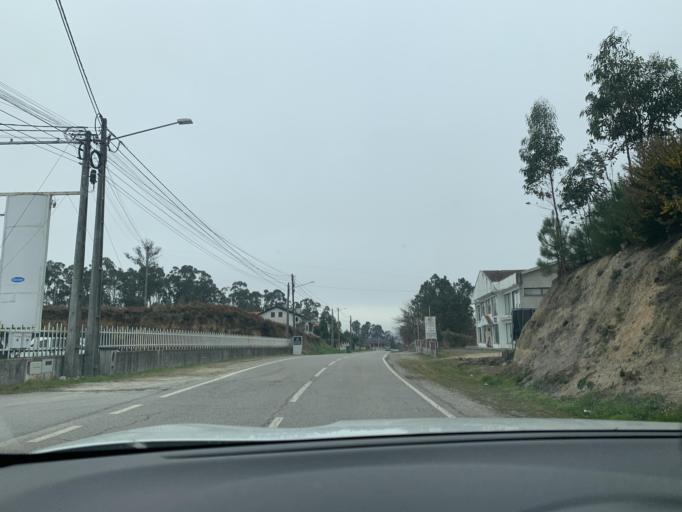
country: PT
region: Viseu
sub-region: Concelho de Tondela
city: Tondela
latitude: 40.5305
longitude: -8.0562
